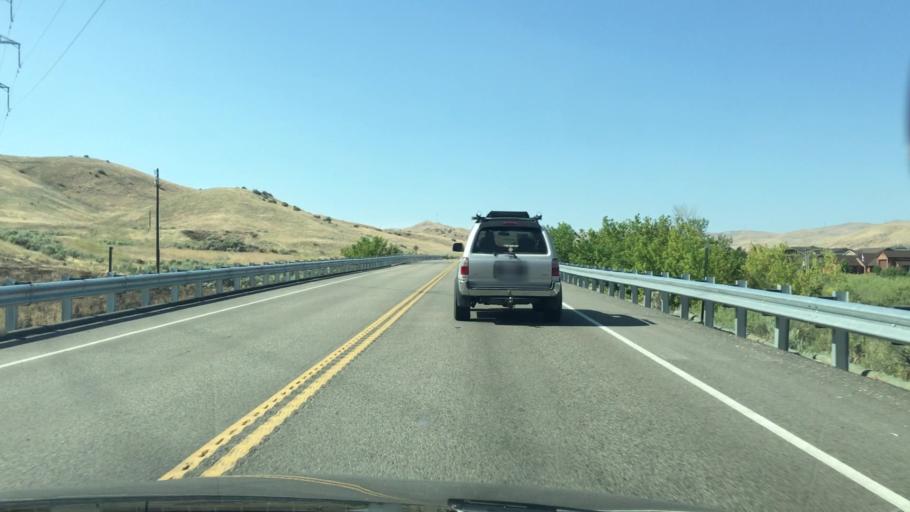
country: US
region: Idaho
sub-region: Ada County
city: Eagle
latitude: 43.7645
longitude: -116.2654
